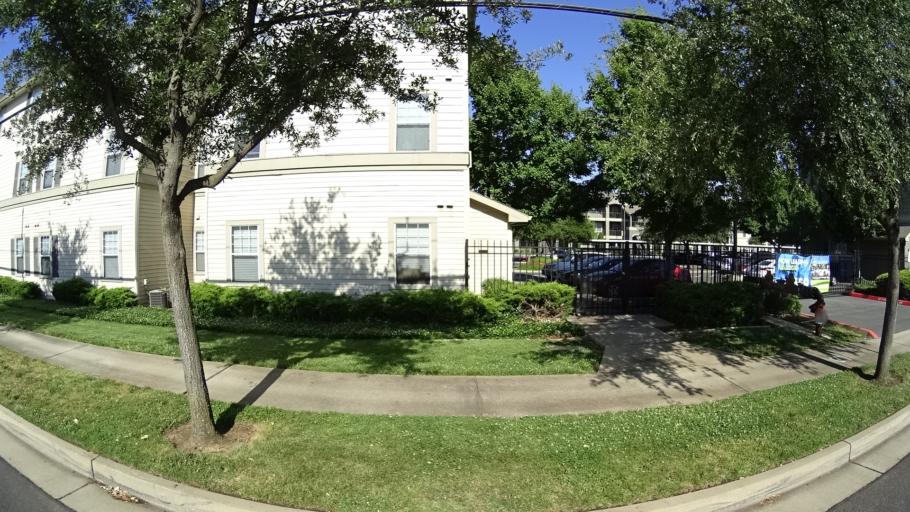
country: US
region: California
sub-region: Sacramento County
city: Florin
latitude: 38.5475
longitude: -121.4231
